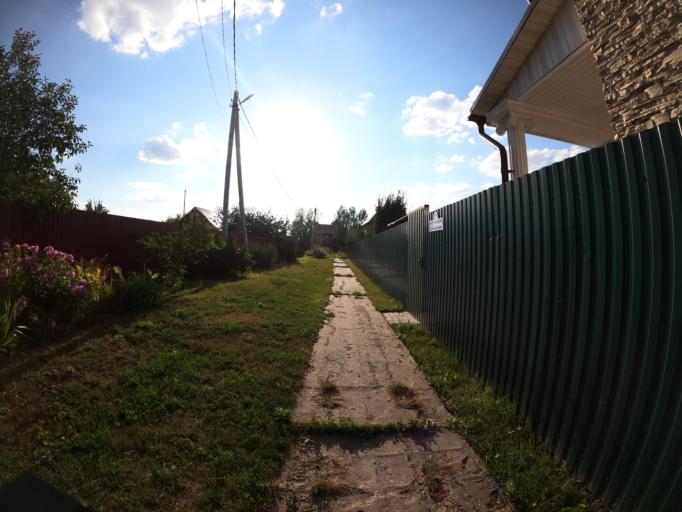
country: RU
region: Moskovskaya
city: Raduzhnyy
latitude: 55.1487
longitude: 38.7348
